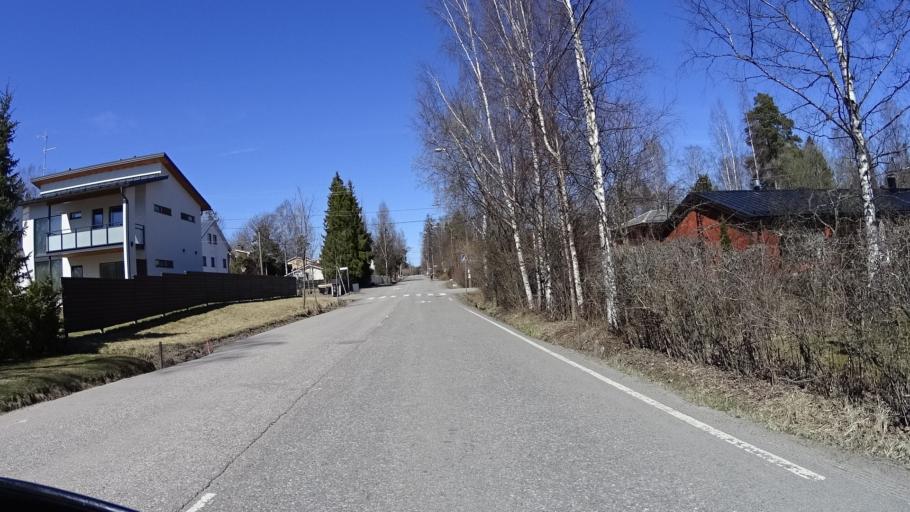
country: FI
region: Uusimaa
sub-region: Helsinki
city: Kilo
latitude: 60.2374
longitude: 24.8136
